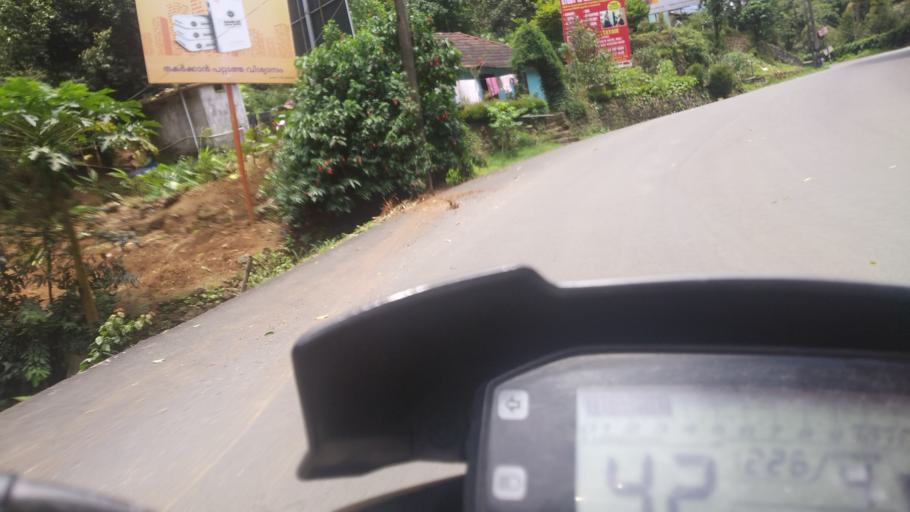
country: IN
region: Kerala
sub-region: Idukki
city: Munnar
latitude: 10.0378
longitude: 76.9953
